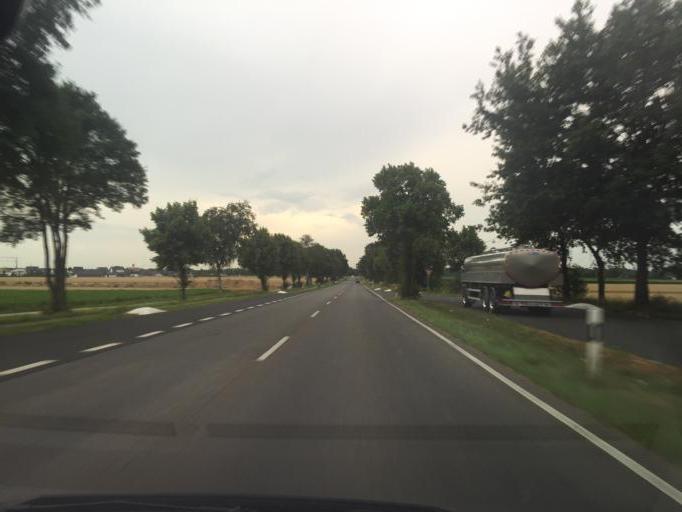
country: DE
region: North Rhine-Westphalia
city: Erkelenz
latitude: 51.1021
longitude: 6.3243
